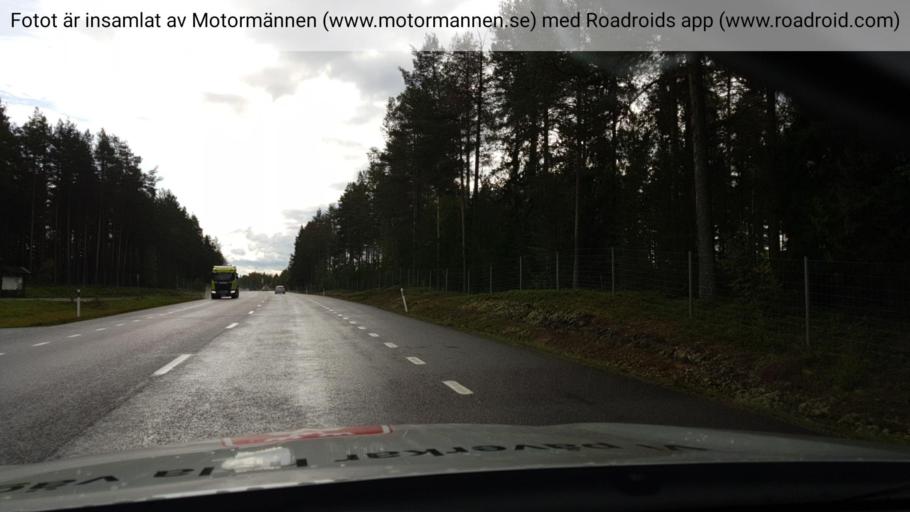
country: SE
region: Norrbotten
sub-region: Bodens Kommun
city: Saevast
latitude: 65.7505
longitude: 21.7660
